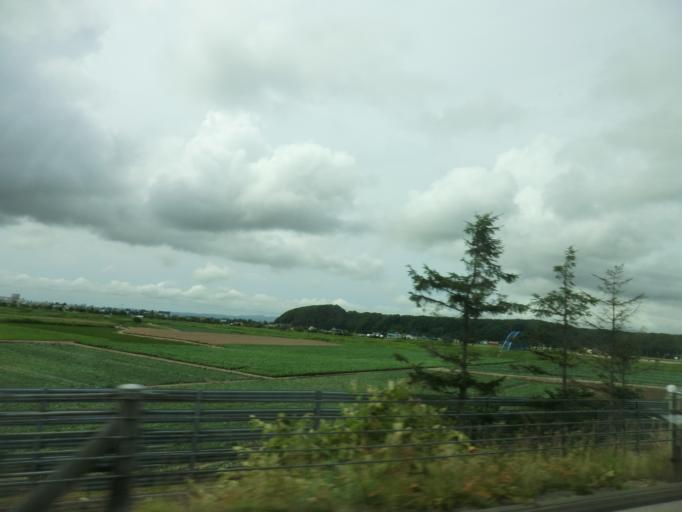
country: JP
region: Hokkaido
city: Iwamizawa
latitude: 43.2373
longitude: 141.8303
